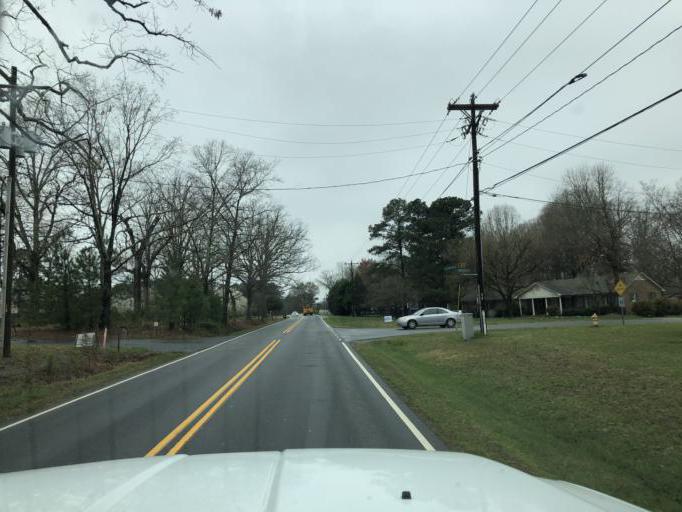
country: US
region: North Carolina
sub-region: Gaston County
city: Mount Holly
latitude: 35.3358
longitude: -80.9241
